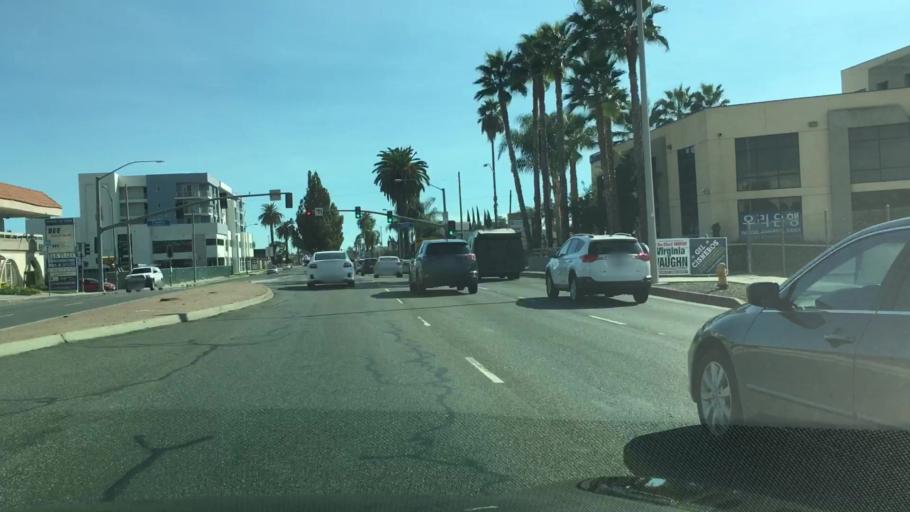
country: US
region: California
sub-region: Orange County
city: Buena Park
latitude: 33.8776
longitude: -117.9984
